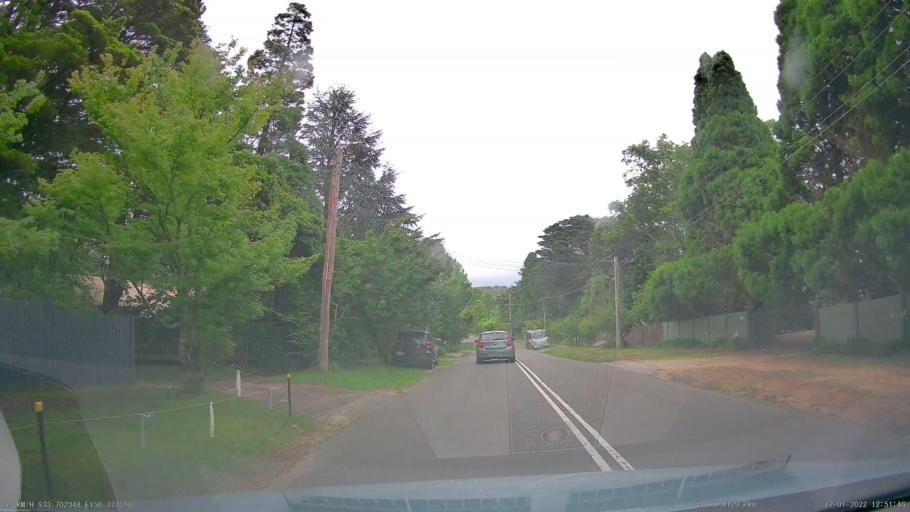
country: AU
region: New South Wales
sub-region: Blue Mountains Municipality
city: Leura
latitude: -33.7021
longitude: 150.3735
